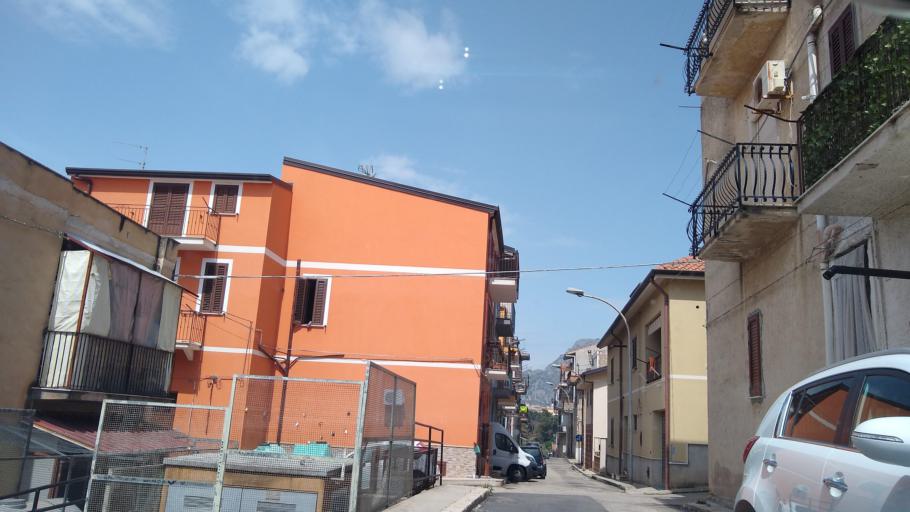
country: IT
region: Sicily
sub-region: Palermo
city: San Cipirello
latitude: 37.9633
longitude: 13.1744
